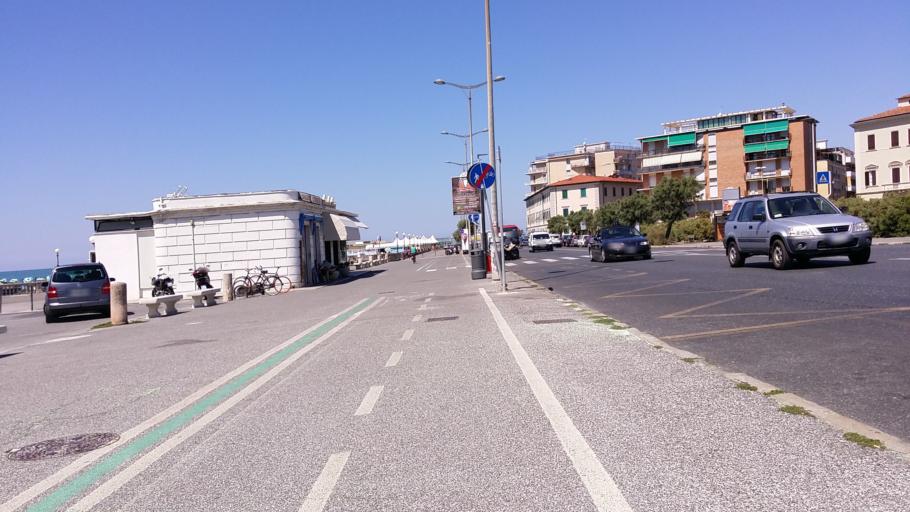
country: IT
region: Tuscany
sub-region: Provincia di Livorno
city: Livorno
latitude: 43.5300
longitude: 10.3063
